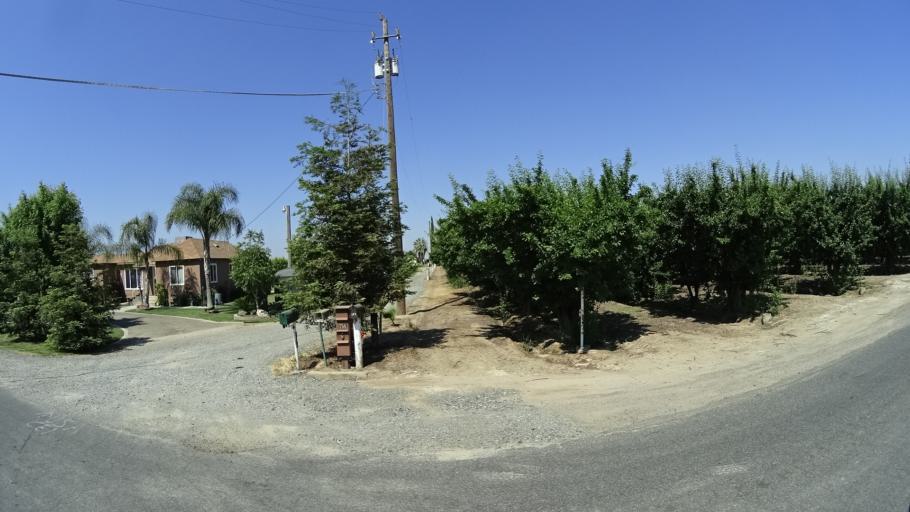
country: US
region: California
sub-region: Fresno County
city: Kingsburg
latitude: 36.4631
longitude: -119.5509
